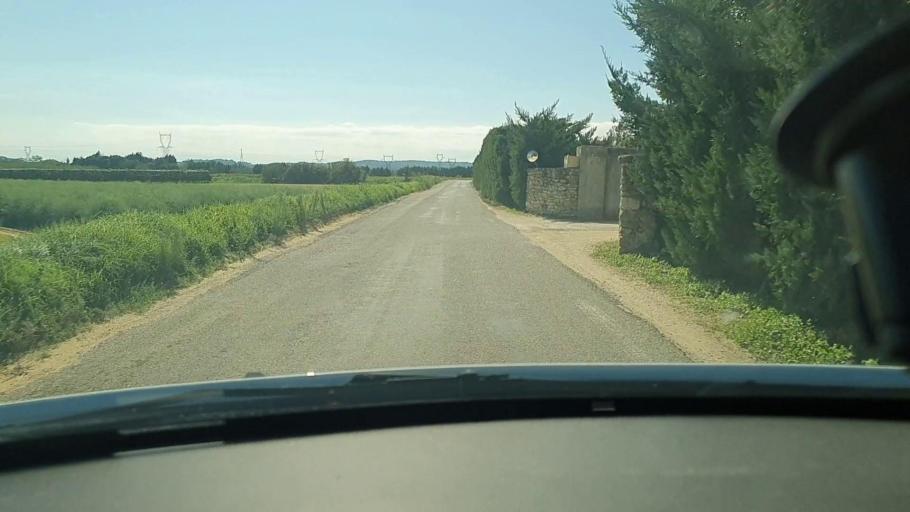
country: FR
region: Languedoc-Roussillon
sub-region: Departement du Gard
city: Saint-Julien-de-Peyrolas
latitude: 44.2877
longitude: 4.5710
